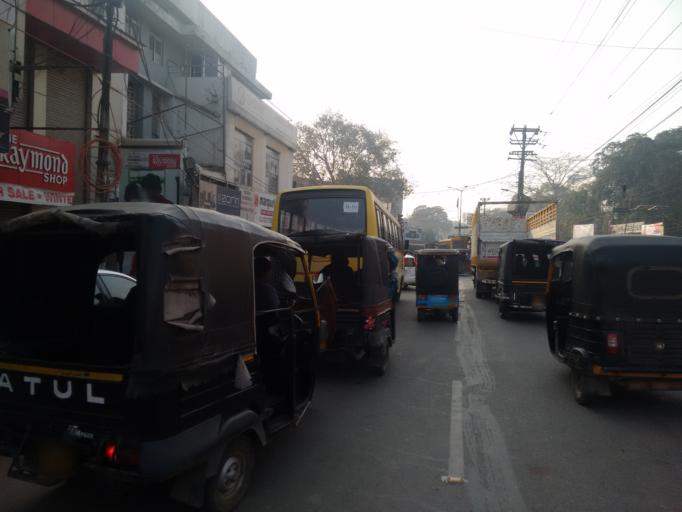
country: IN
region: Jharkhand
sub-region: Ranchi
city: Ranchi
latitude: 23.3543
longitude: 85.3243
